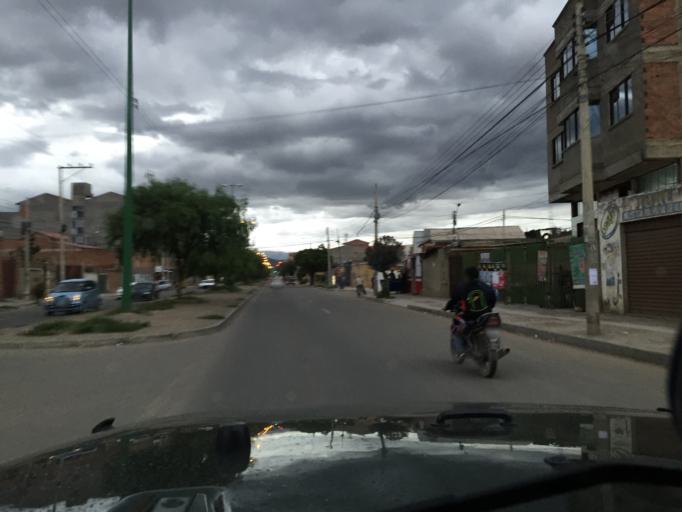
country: BO
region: Cochabamba
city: Cochabamba
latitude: -17.3971
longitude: -66.1960
